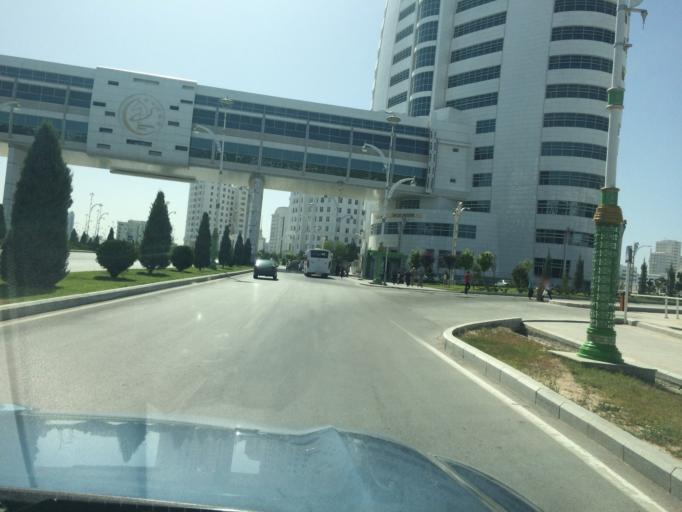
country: TM
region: Ahal
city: Ashgabat
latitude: 37.8963
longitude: 58.3714
